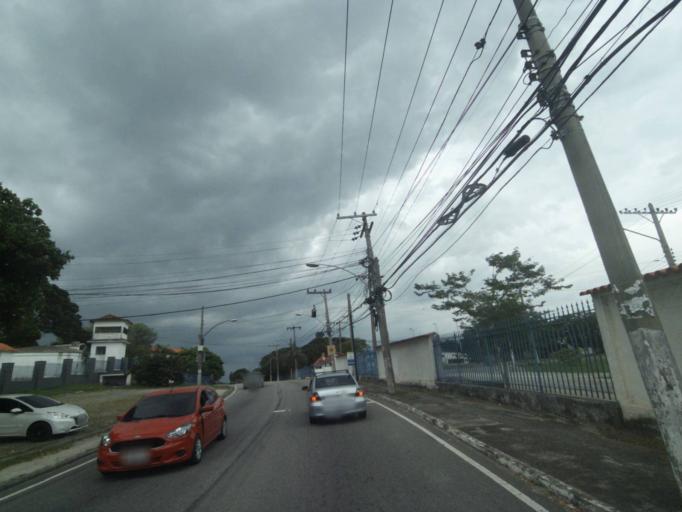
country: BR
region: Rio de Janeiro
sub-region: Sao Joao De Meriti
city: Sao Joao de Meriti
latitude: -22.8825
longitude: -43.3829
